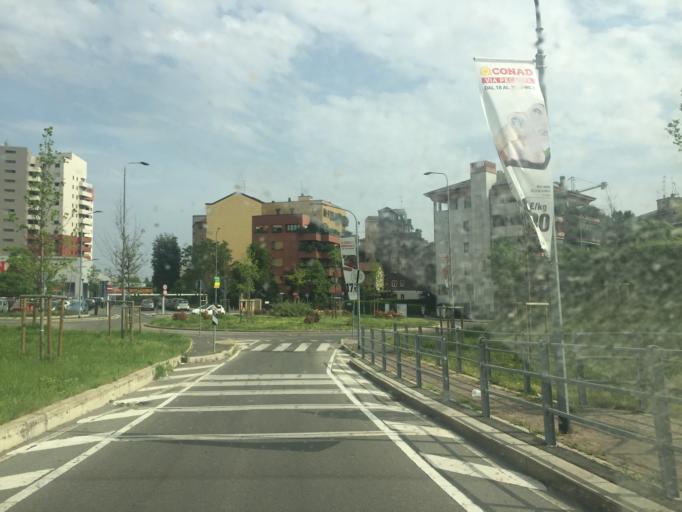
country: IT
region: Lombardy
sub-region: Citta metropolitana di Milano
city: Novate Milanese
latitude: 45.4959
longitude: 9.1619
